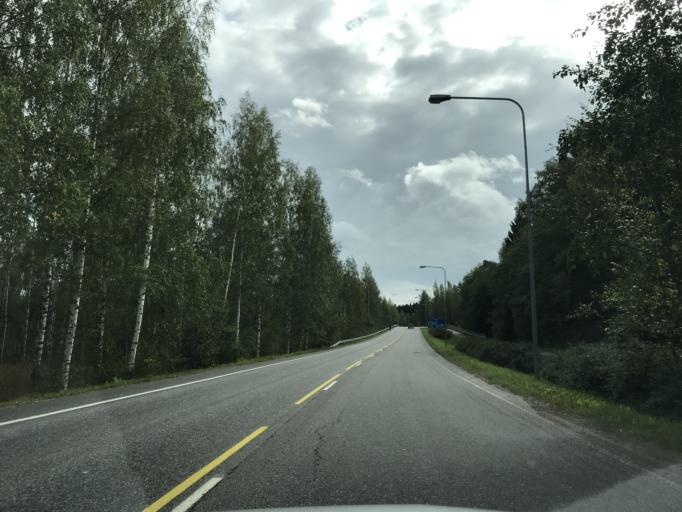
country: FI
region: Paijanne Tavastia
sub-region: Lahti
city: Lahti
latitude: 61.0010
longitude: 25.7784
